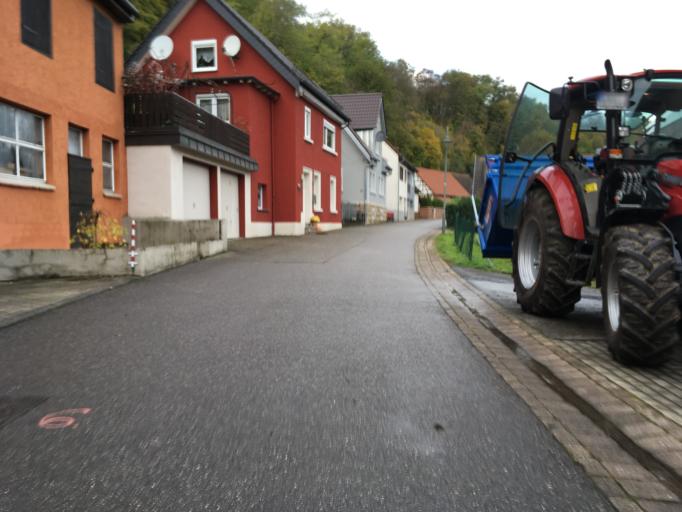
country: DE
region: Baden-Wuerttemberg
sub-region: Regierungsbezirk Stuttgart
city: Widdern
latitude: 49.3199
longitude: 9.4194
